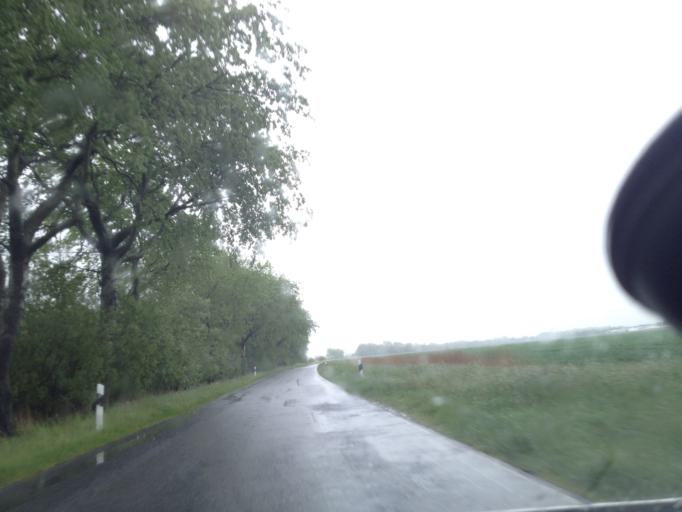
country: DE
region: Schleswig-Holstein
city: Rodenas
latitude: 54.8838
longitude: 8.7201
